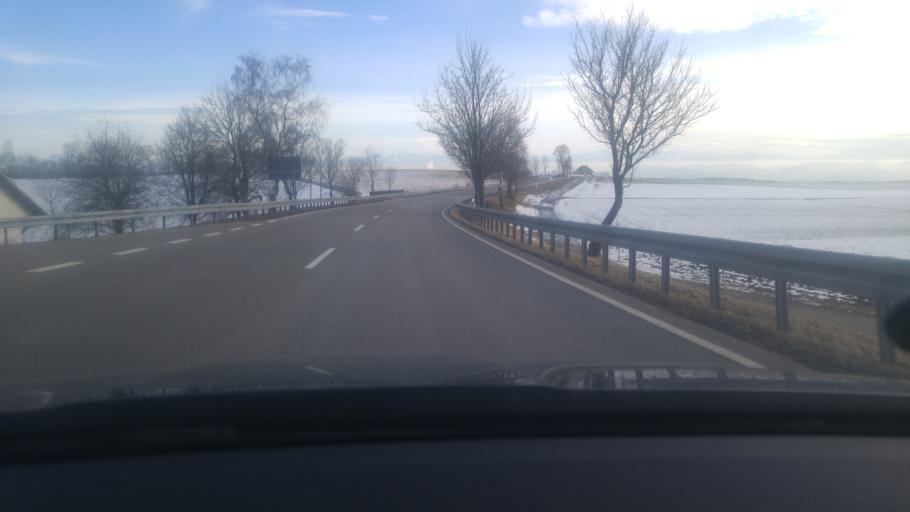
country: DE
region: Baden-Wuerttemberg
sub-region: Freiburg Region
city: Hochenschwand
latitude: 47.7007
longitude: 8.1453
